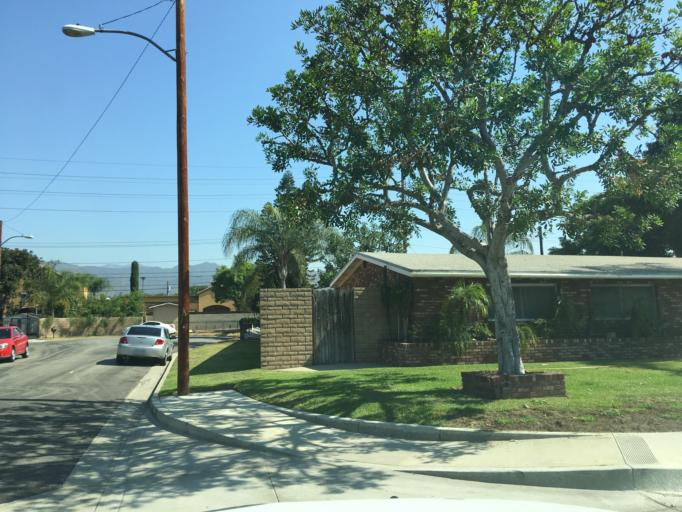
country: US
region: California
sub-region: Los Angeles County
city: Citrus
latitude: 34.1135
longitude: -117.9046
